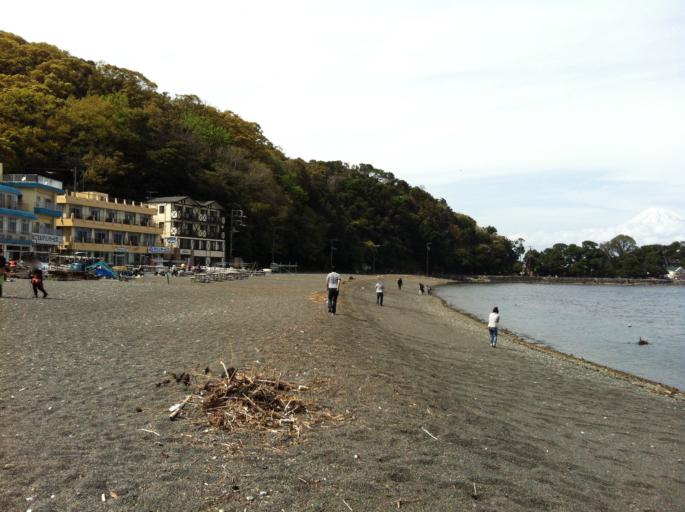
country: JP
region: Shizuoka
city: Heda
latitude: 35.0243
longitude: 138.7869
